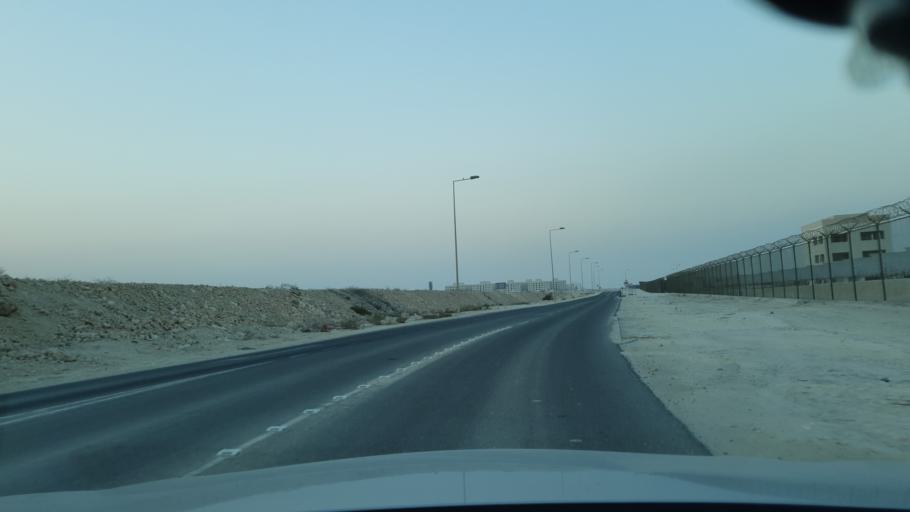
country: BH
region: Central Governorate
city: Dar Kulayb
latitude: 25.9728
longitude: 50.6096
